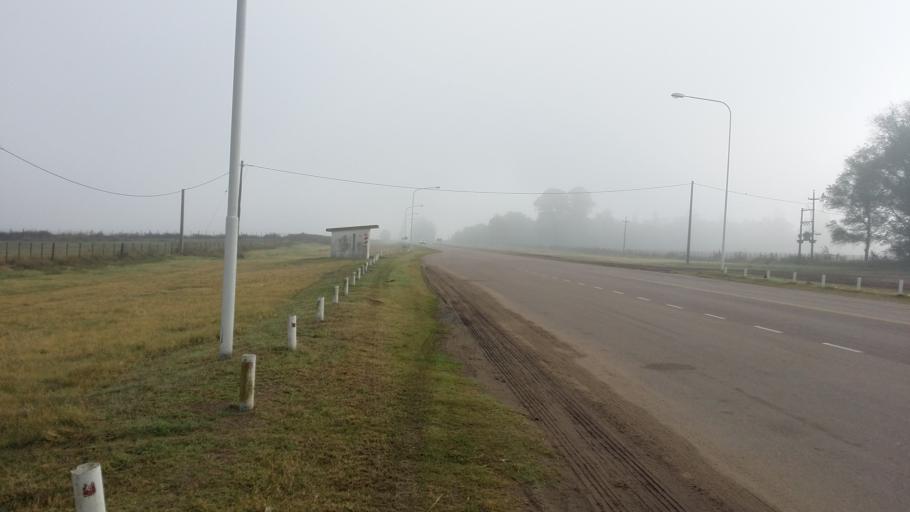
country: AR
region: La Pampa
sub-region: Departamento de Quemu Quemu
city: Quemu Quemu
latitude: -36.0642
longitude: -63.5848
